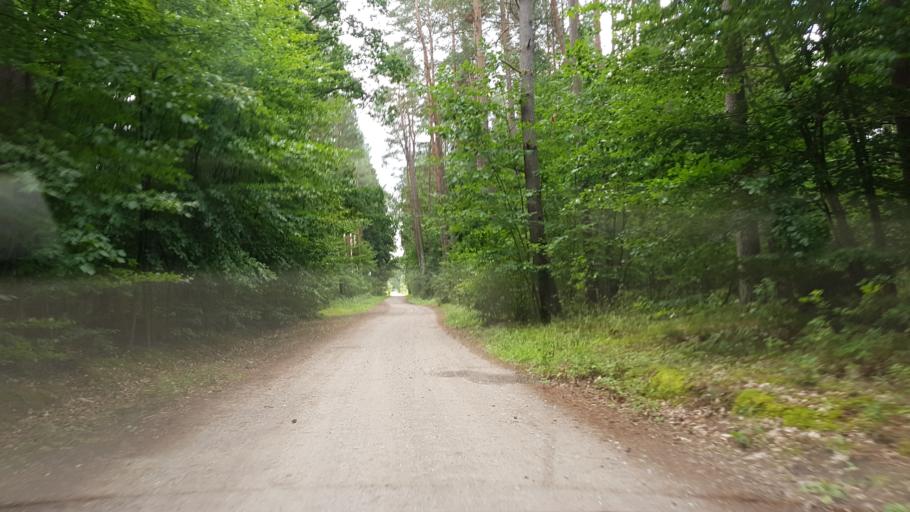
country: PL
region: West Pomeranian Voivodeship
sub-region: Powiat bialogardzki
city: Tychowo
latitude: 54.0009
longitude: 16.3039
